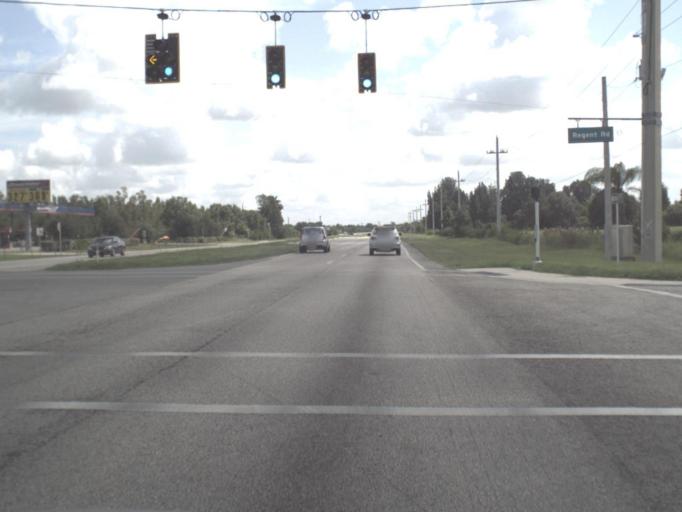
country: US
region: Florida
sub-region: Charlotte County
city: Cleveland
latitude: 26.9433
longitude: -82.0105
